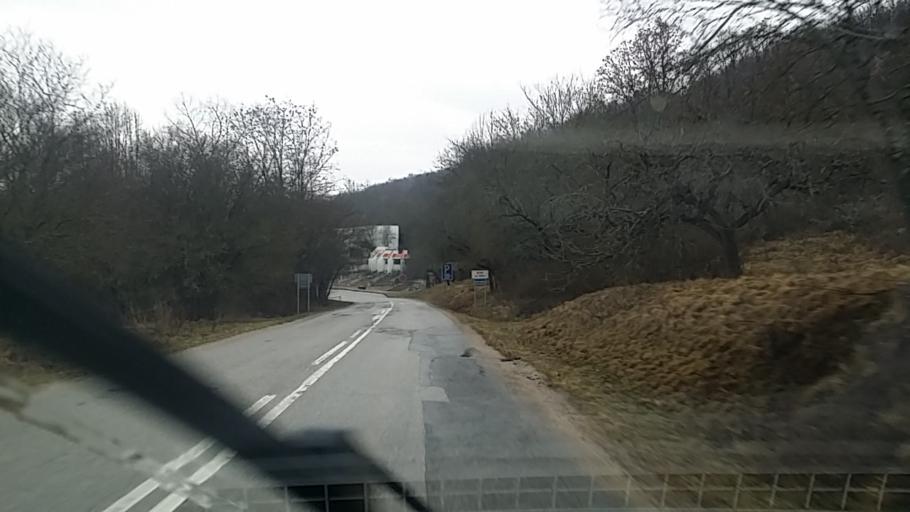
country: HU
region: Borsod-Abauj-Zemplen
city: Putnok
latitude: 48.4770
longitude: 20.4720
